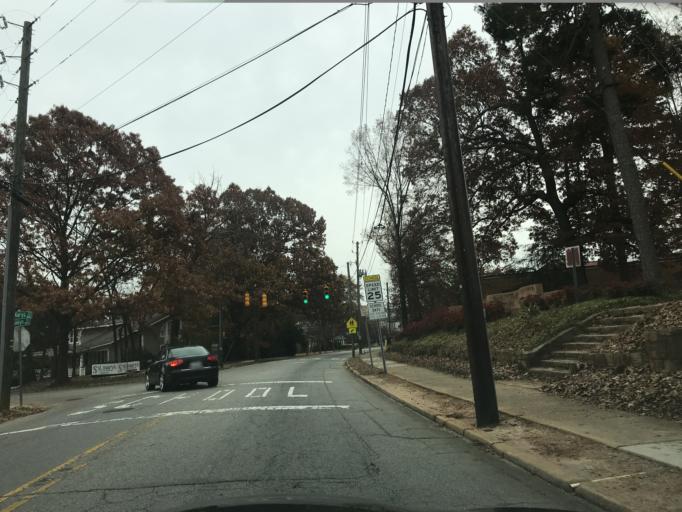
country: US
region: North Carolina
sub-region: Wake County
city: West Raleigh
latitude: 35.7914
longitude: -78.6518
